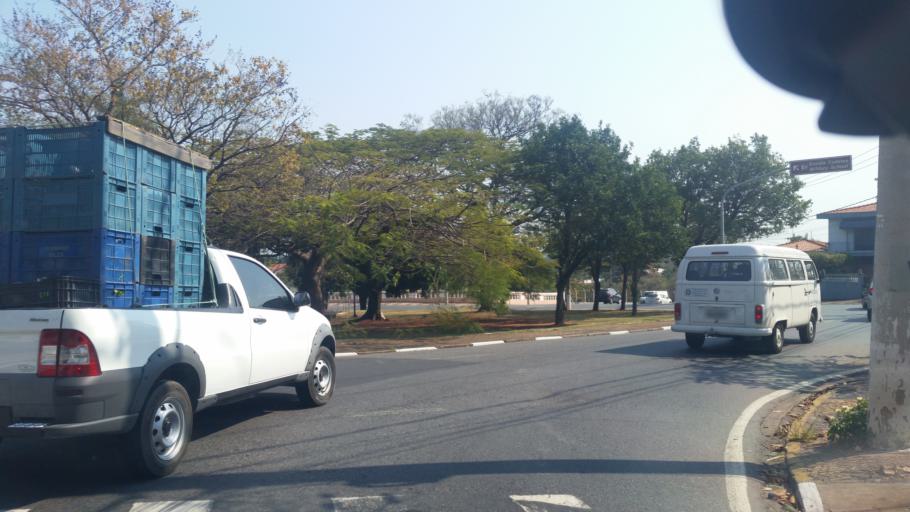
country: BR
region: Sao Paulo
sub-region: Campinas
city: Campinas
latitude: -22.8872
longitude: -47.0783
